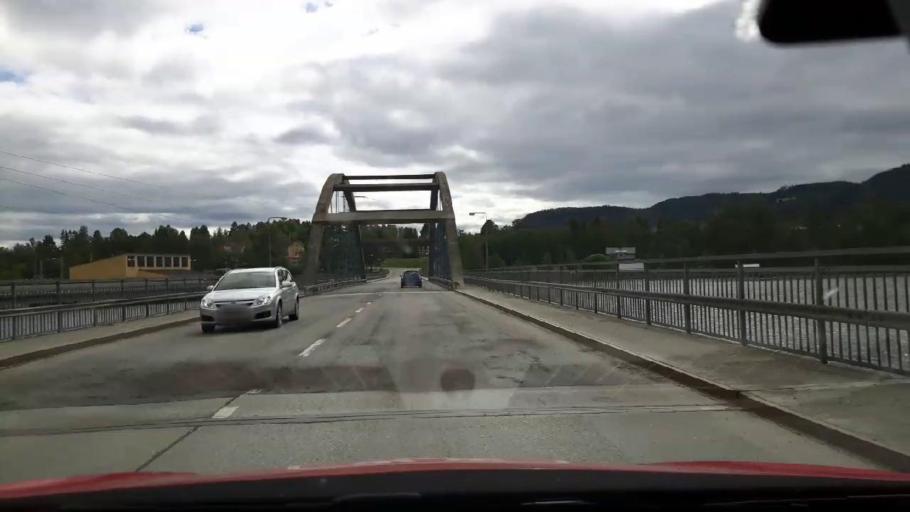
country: SE
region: Jaemtland
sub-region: Ragunda Kommun
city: Hammarstrand
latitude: 63.1144
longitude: 16.3557
